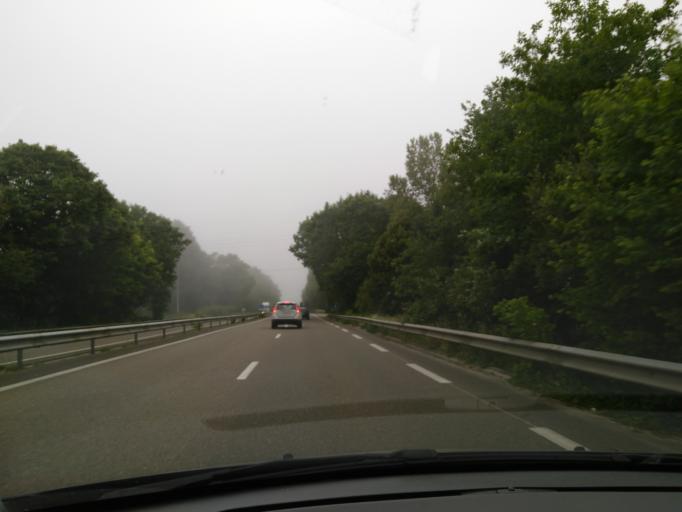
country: FR
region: Aquitaine
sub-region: Departement des Landes
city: Tartas
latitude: 43.8255
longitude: -0.8243
